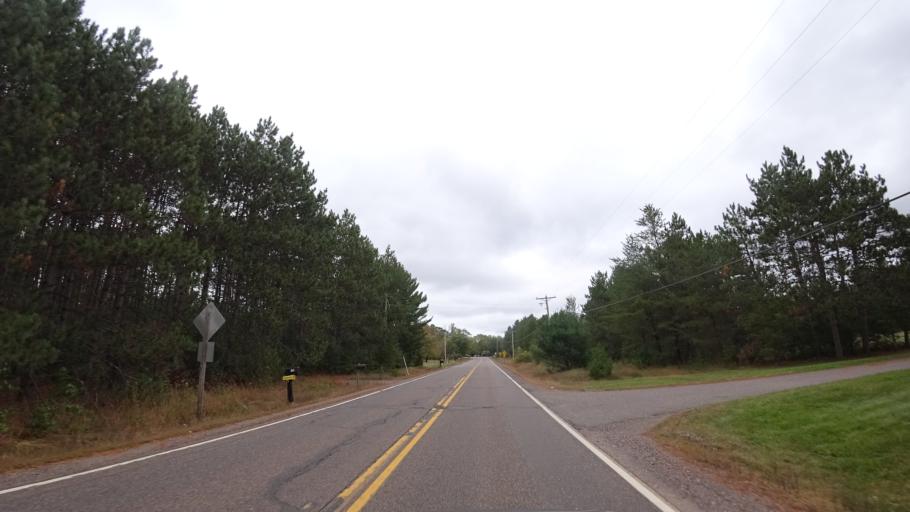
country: US
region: Wisconsin
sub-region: Chippewa County
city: Lake Wissota
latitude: 44.9459
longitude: -91.2628
